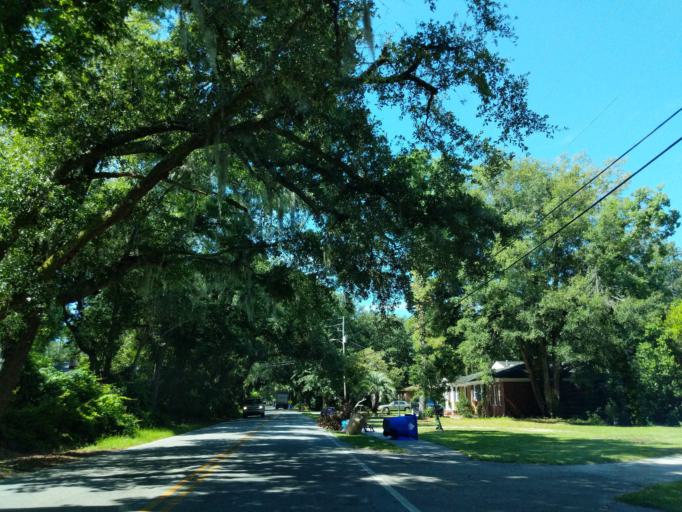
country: US
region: South Carolina
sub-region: Charleston County
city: Charleston
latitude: 32.7358
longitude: -79.9237
